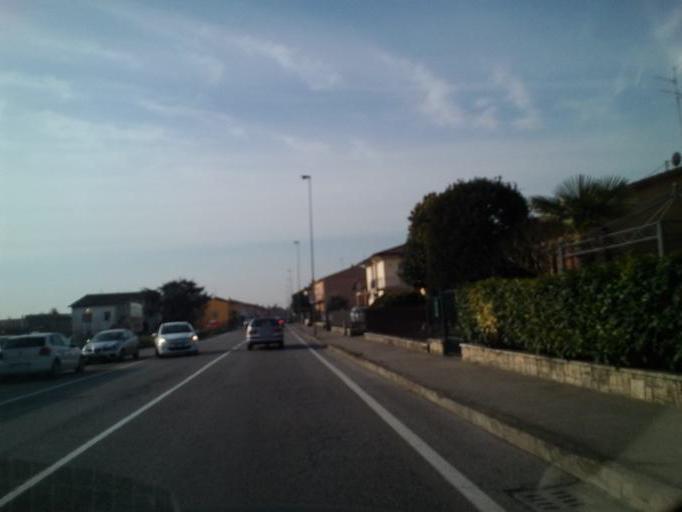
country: IT
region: Veneto
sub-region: Provincia di Verona
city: Mozzecane
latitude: 45.3293
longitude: 10.8341
